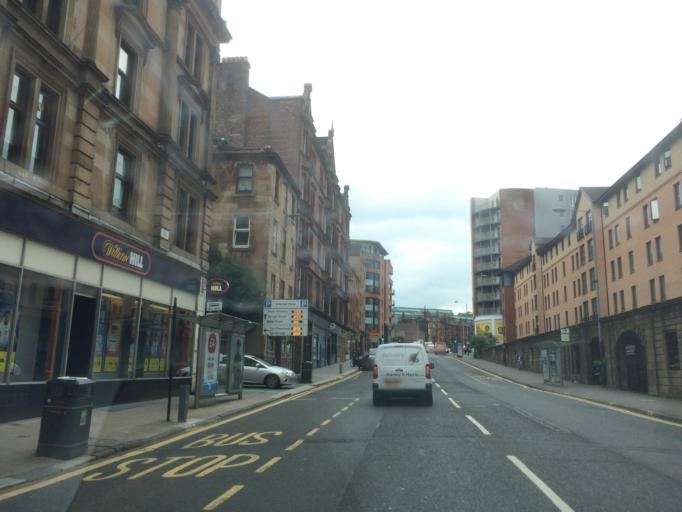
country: GB
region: Scotland
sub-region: Glasgow City
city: Glasgow
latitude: 55.8579
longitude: -4.2425
